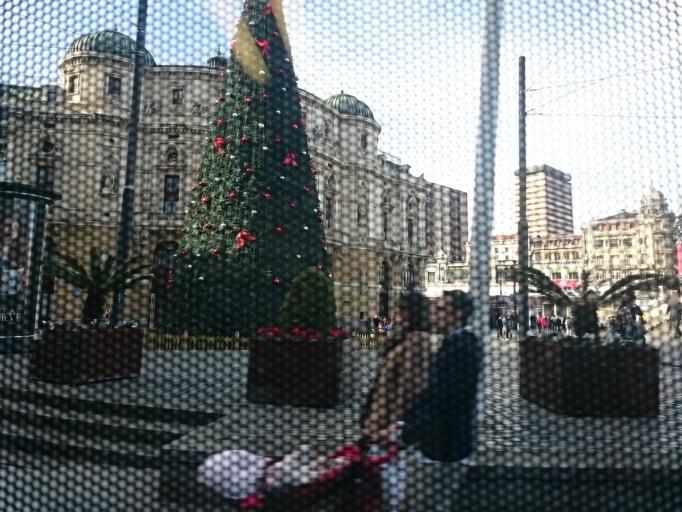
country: ES
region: Basque Country
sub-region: Bizkaia
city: Bilbao
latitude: 43.2596
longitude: -2.9242
